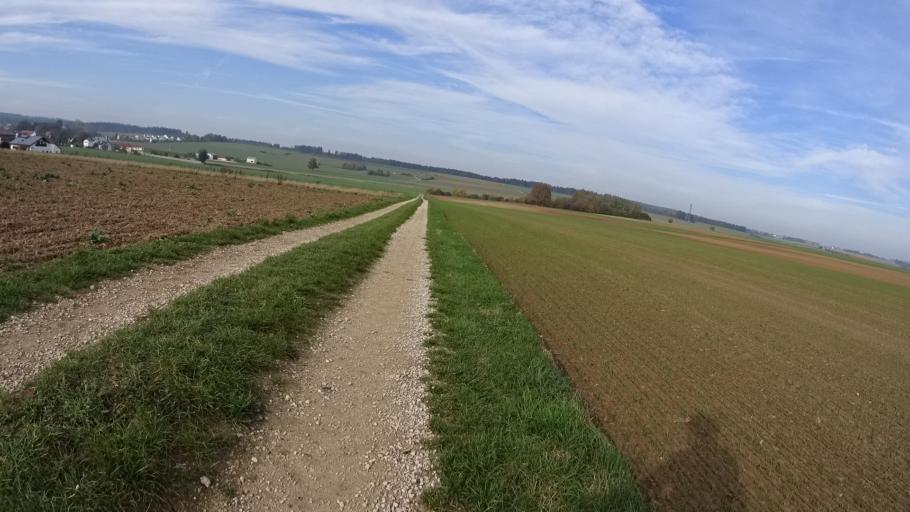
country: DE
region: Bavaria
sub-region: Upper Bavaria
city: Buxheim
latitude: 48.8213
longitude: 11.2839
